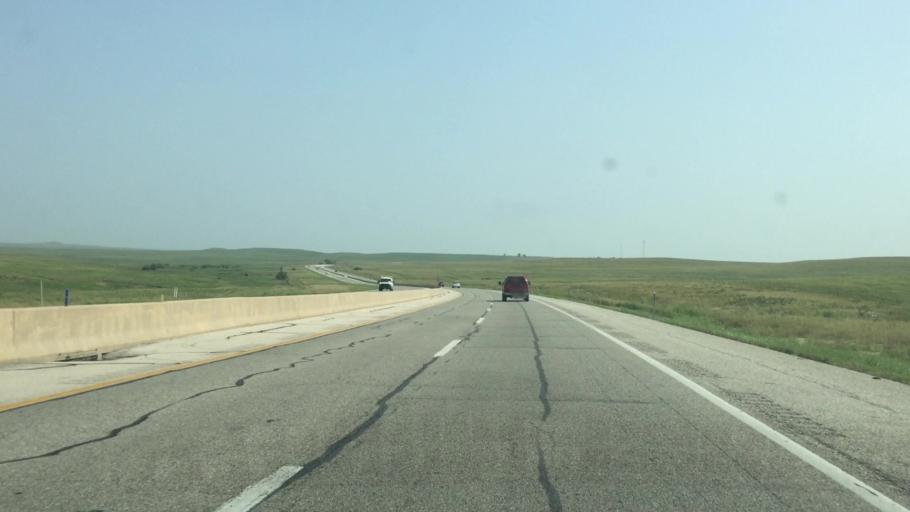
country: US
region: Kansas
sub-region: Chase County
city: Cottonwood Falls
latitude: 38.2399
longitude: -96.3956
